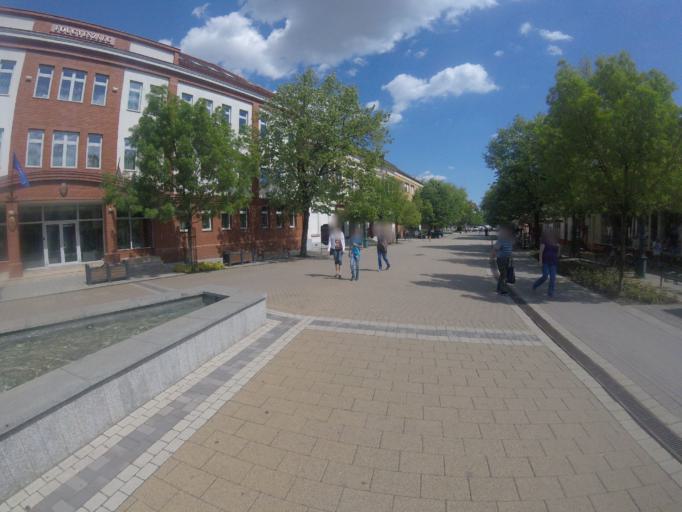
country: HU
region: Bekes
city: Gyula
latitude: 46.6452
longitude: 21.2736
